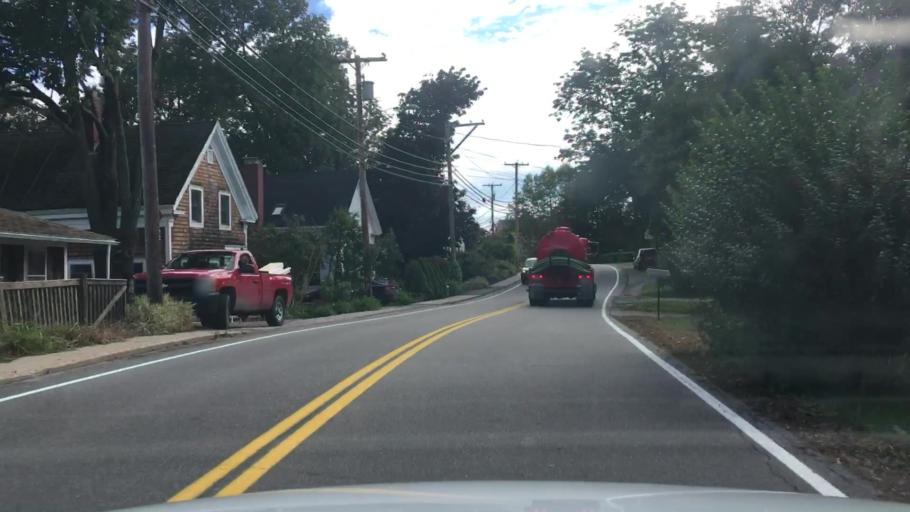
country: US
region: Maine
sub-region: York County
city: Kittery Point
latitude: 43.0833
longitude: -70.7015
